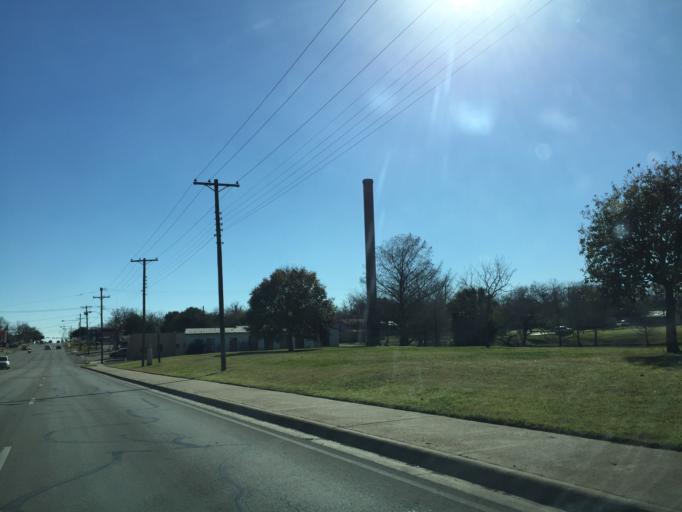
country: US
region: Texas
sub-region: Williamson County
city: Taylor
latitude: 30.5791
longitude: -97.4106
